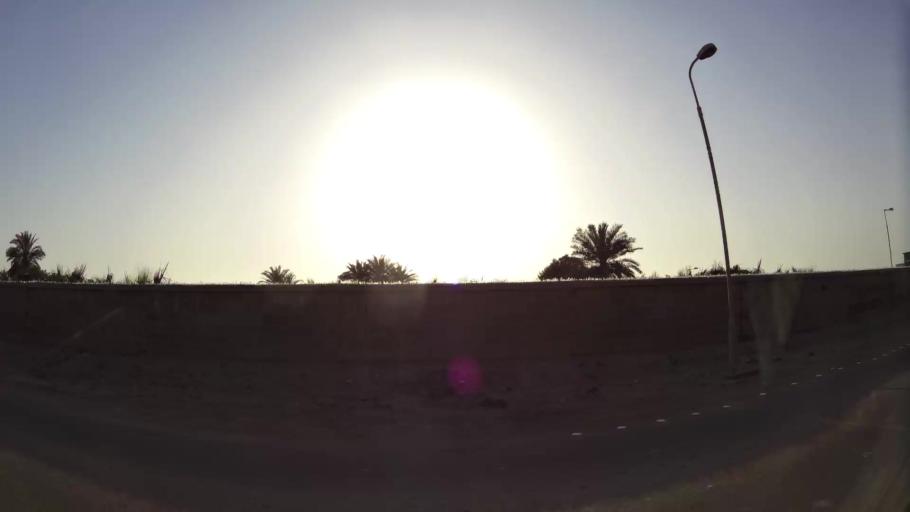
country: BH
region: Manama
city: Jidd Hafs
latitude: 26.2062
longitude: 50.4709
